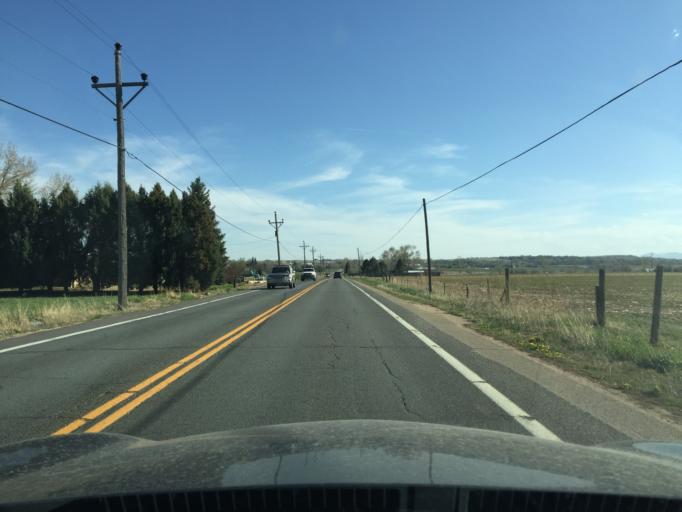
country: US
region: Colorado
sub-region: Boulder County
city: Niwot
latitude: 40.1225
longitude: -105.1310
